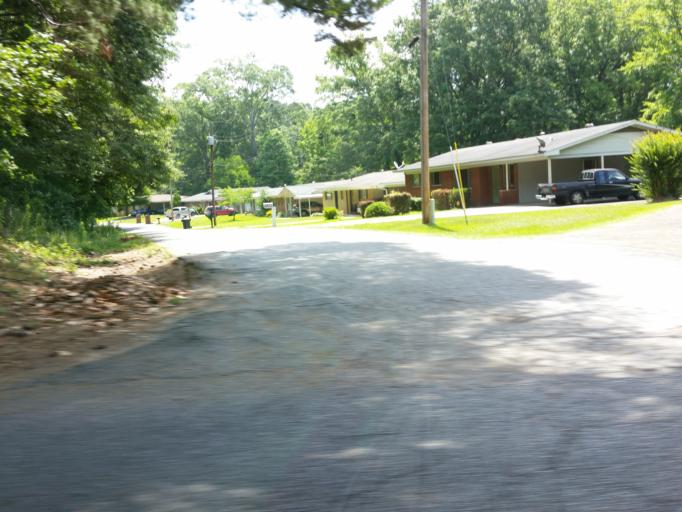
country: US
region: Mississippi
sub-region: Lauderdale County
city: Meridian
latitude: 32.3882
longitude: -88.7166
